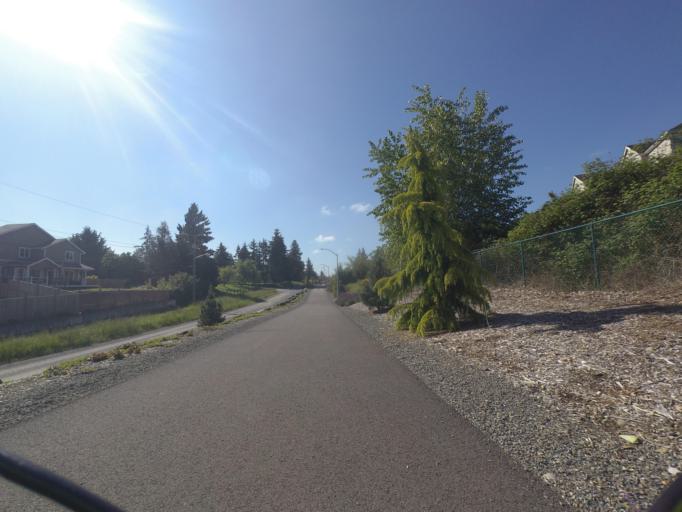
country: US
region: Washington
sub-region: Pierce County
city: Tacoma
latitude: 47.2193
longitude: -122.4157
